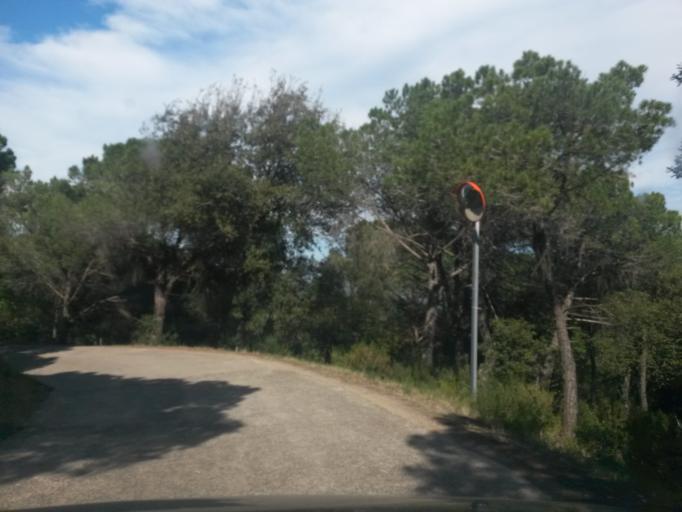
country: ES
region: Catalonia
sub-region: Provincia de Girona
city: Brunyola
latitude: 41.9049
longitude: 2.6873
